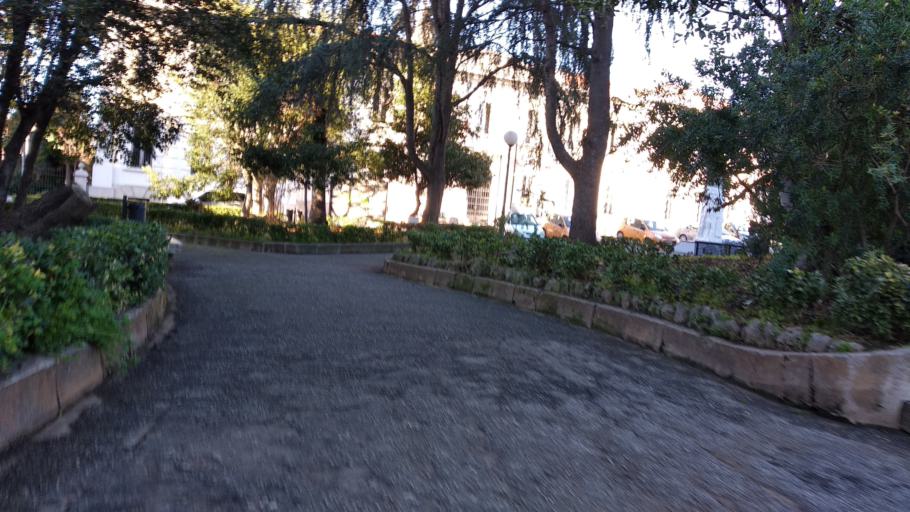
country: IT
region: Calabria
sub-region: Provincia di Reggio Calabria
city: Seminara
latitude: 38.3583
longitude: 15.8492
